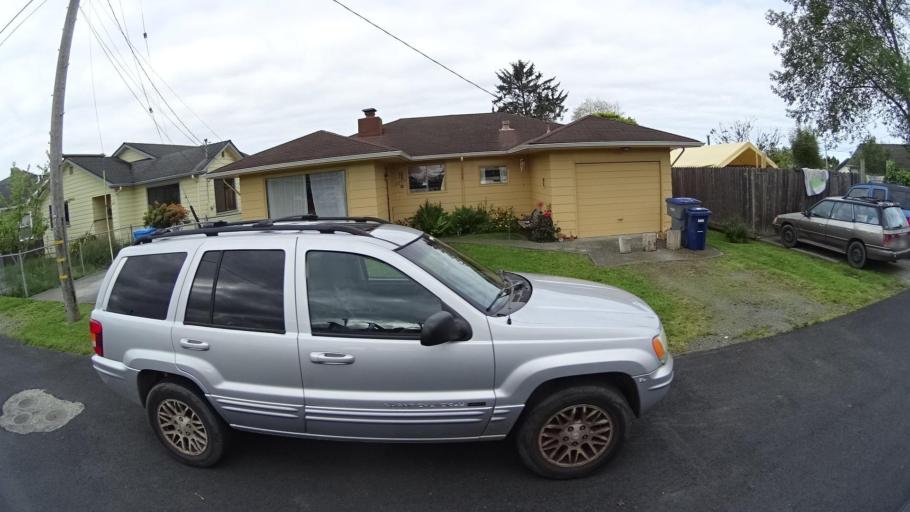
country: US
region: California
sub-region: Humboldt County
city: Arcata
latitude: 40.8812
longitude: -124.0901
